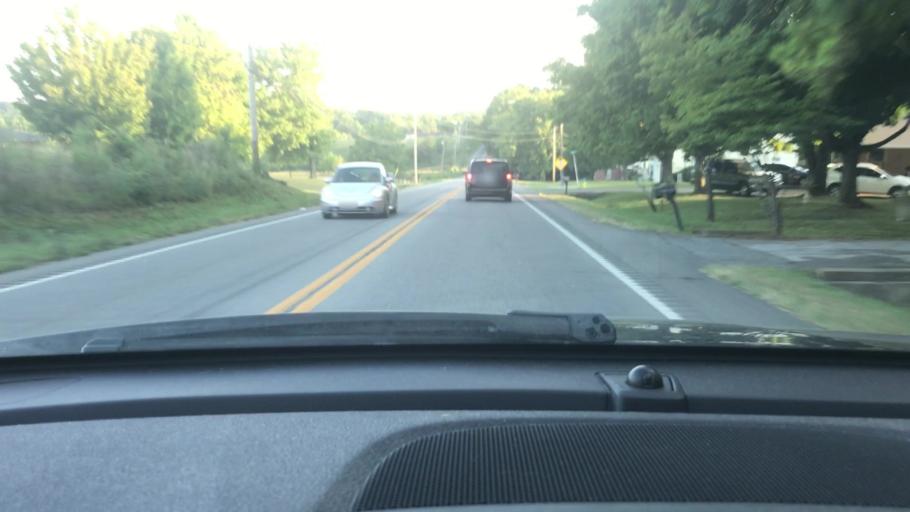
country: US
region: Tennessee
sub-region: Dickson County
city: Dickson
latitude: 36.0918
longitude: -87.3765
